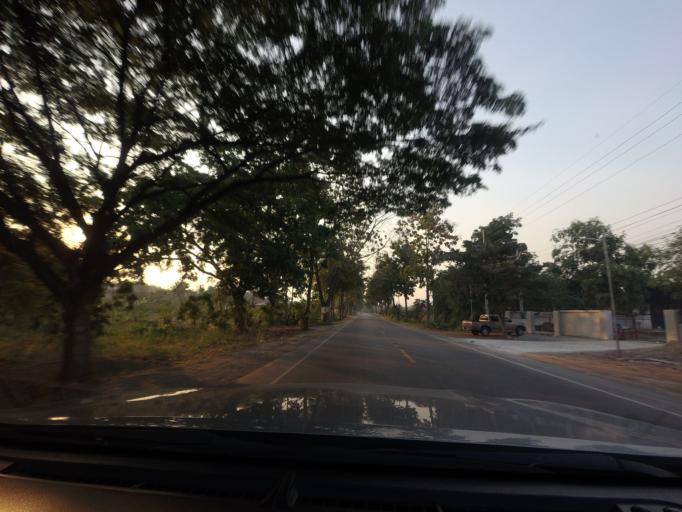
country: TH
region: Phitsanulok
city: Wang Thong
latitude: 16.7133
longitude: 100.4731
